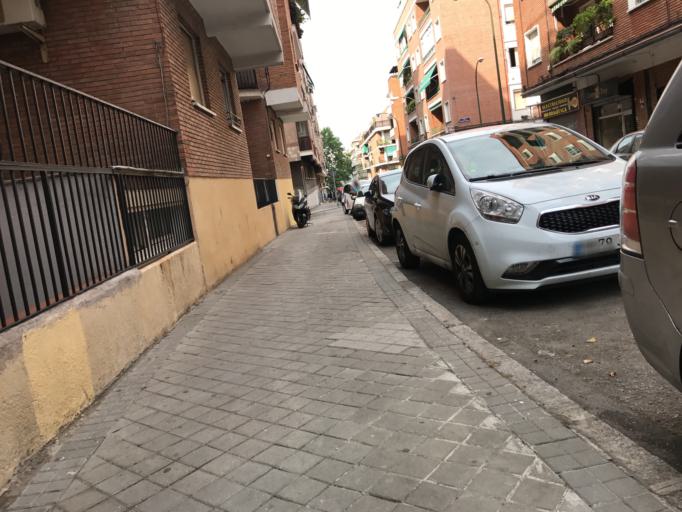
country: ES
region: Madrid
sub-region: Provincia de Madrid
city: Salamanca
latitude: 40.4437
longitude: -3.6695
